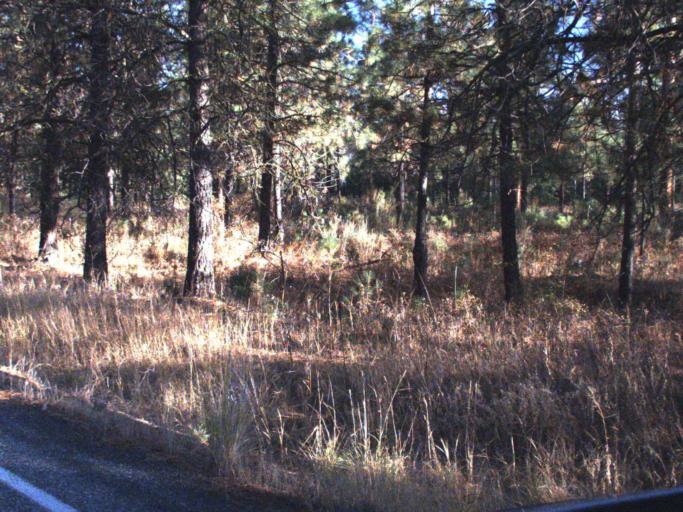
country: US
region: Washington
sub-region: Okanogan County
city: Coulee Dam
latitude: 48.0524
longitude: -118.6697
